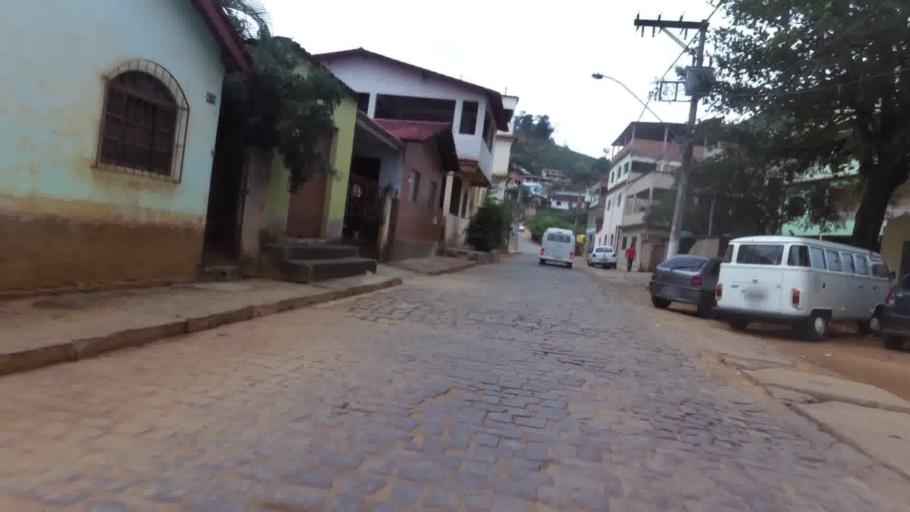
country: BR
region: Espirito Santo
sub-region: Alfredo Chaves
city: Alfredo Chaves
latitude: -20.6364
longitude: -40.7511
